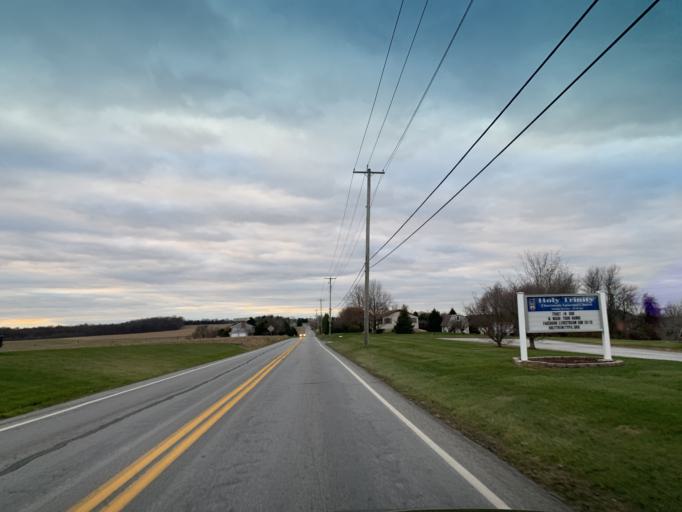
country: US
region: Pennsylvania
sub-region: York County
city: Shrewsbury
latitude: 39.7834
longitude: -76.6403
